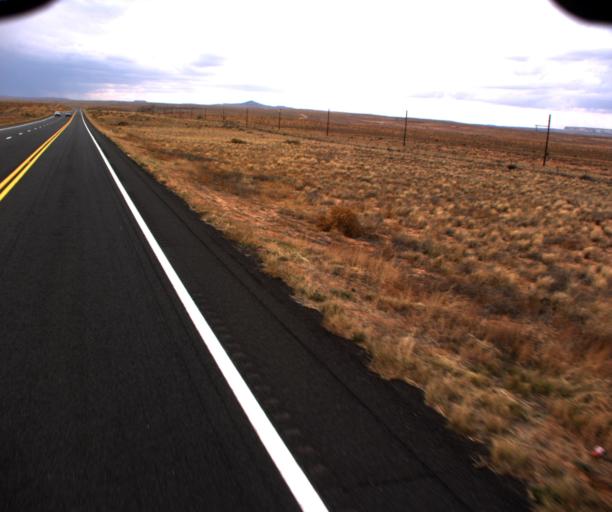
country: US
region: Arizona
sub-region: Coconino County
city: Kaibito
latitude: 36.3991
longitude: -110.8594
